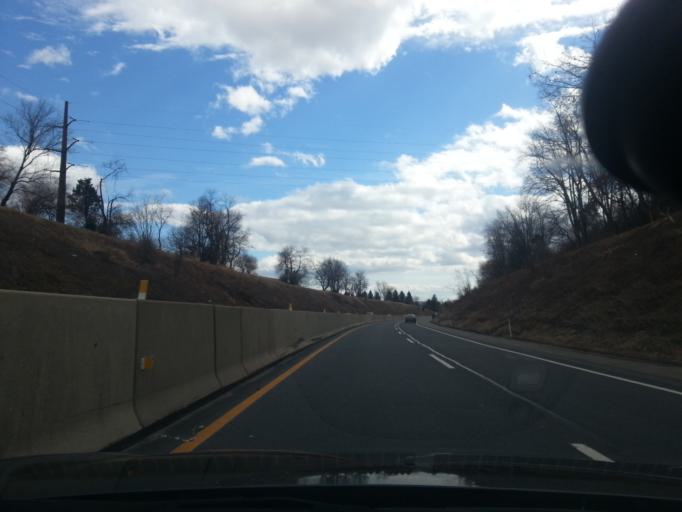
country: US
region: Pennsylvania
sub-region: Lehigh County
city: Schnecksville
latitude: 40.6333
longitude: -75.5777
